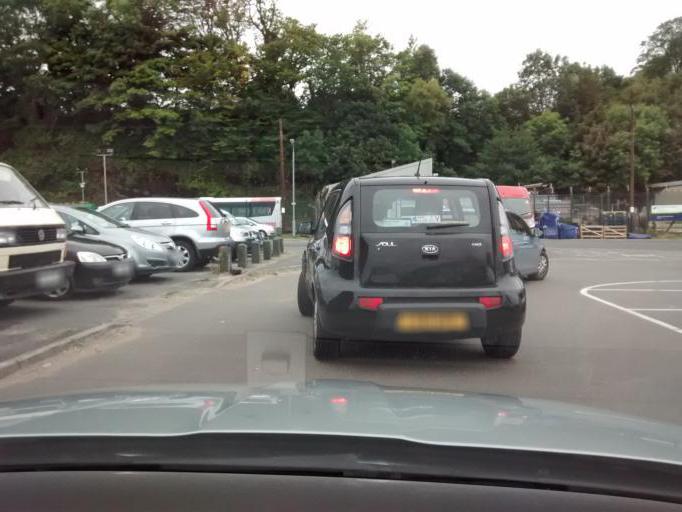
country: GB
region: Scotland
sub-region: North Ayrshire
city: Lamlash
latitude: 55.5765
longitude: -5.1376
